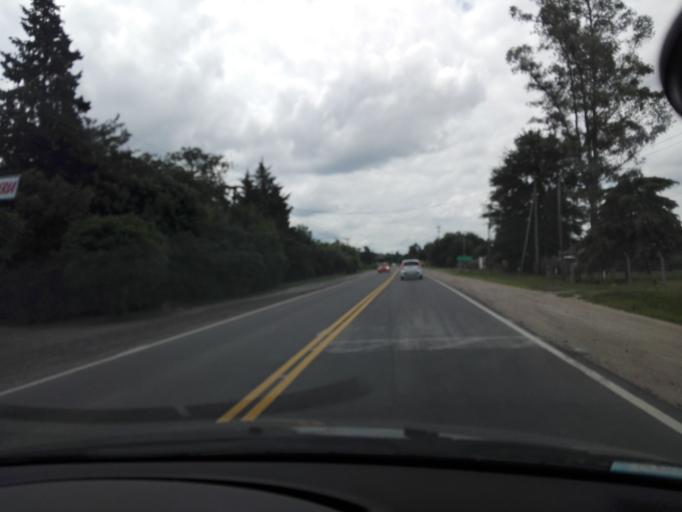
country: AR
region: Cordoba
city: Alta Gracia
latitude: -31.5940
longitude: -64.4546
